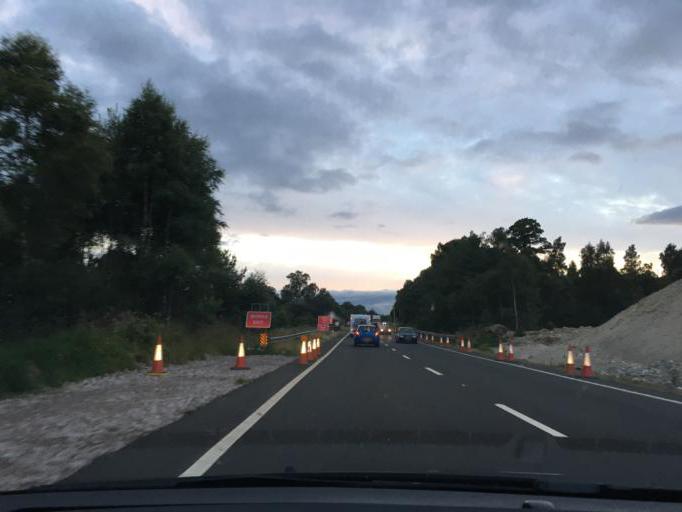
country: GB
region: Scotland
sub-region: Highland
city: Kingussie
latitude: 57.1096
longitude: -3.9624
